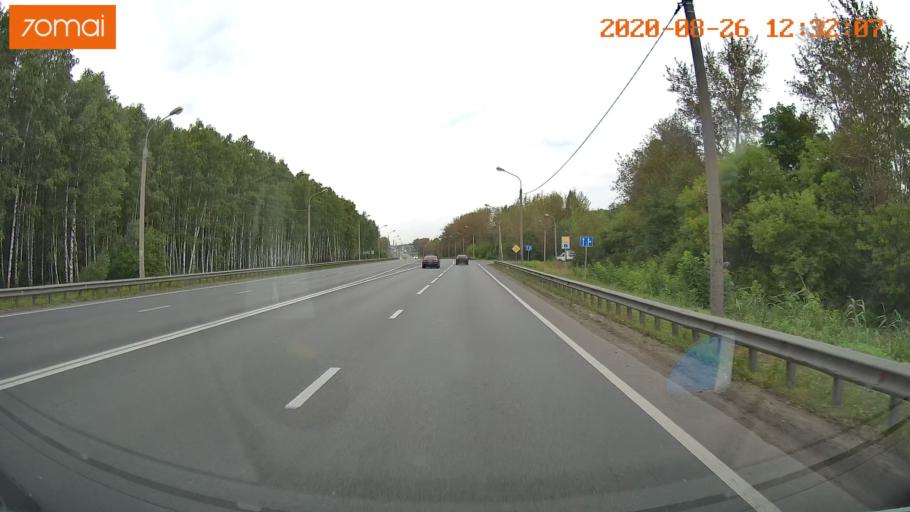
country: RU
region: Rjazan
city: Ryazan'
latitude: 54.5753
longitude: 39.7960
